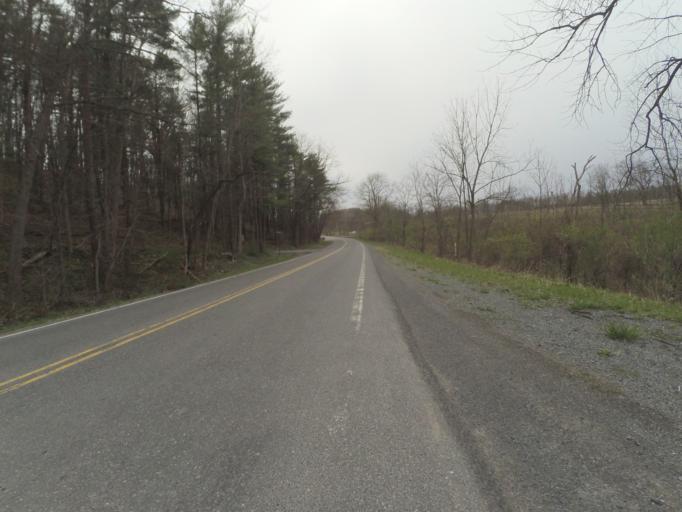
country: US
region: Pennsylvania
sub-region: Centre County
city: Milesburg
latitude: 40.9660
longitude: -77.7414
